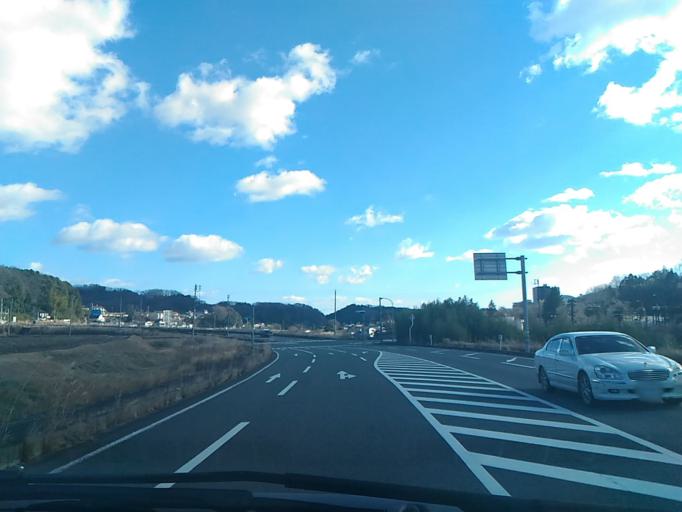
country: JP
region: Fukushima
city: Iwaki
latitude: 36.9971
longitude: 140.8077
